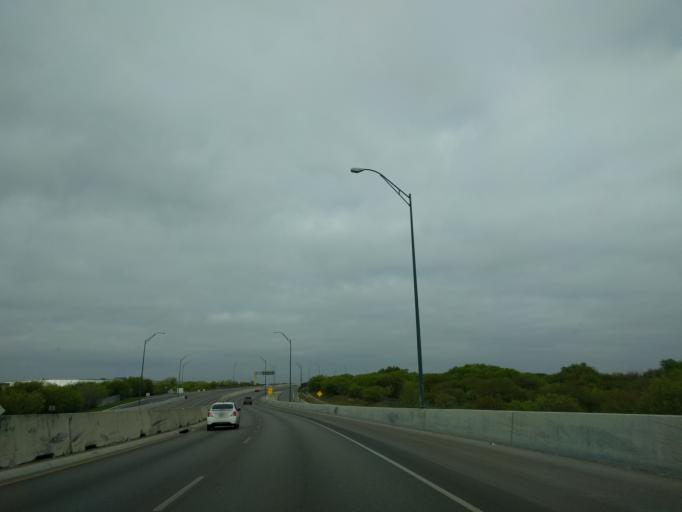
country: US
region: Texas
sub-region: Bexar County
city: Windcrest
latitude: 29.5416
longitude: -98.4227
